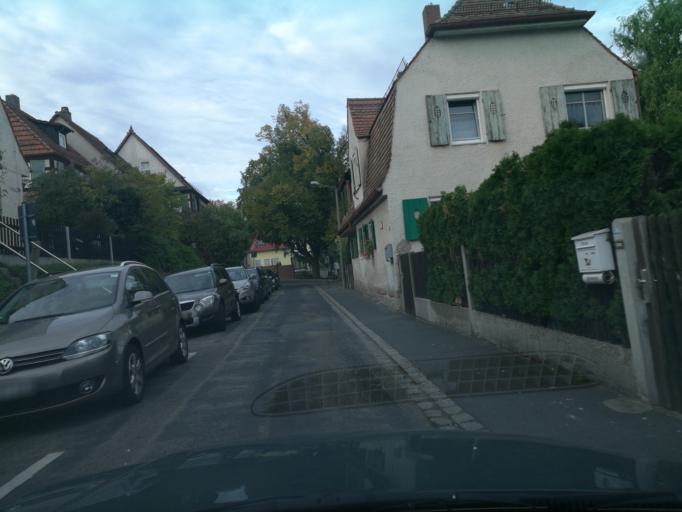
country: DE
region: Bavaria
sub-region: Regierungsbezirk Mittelfranken
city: Furth
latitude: 49.4884
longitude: 10.9781
